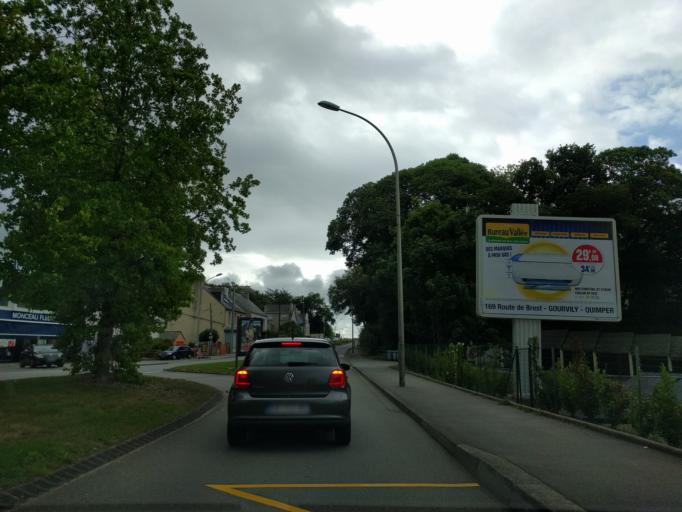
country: FR
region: Brittany
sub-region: Departement du Finistere
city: Quimper
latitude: 47.9872
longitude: -4.1084
